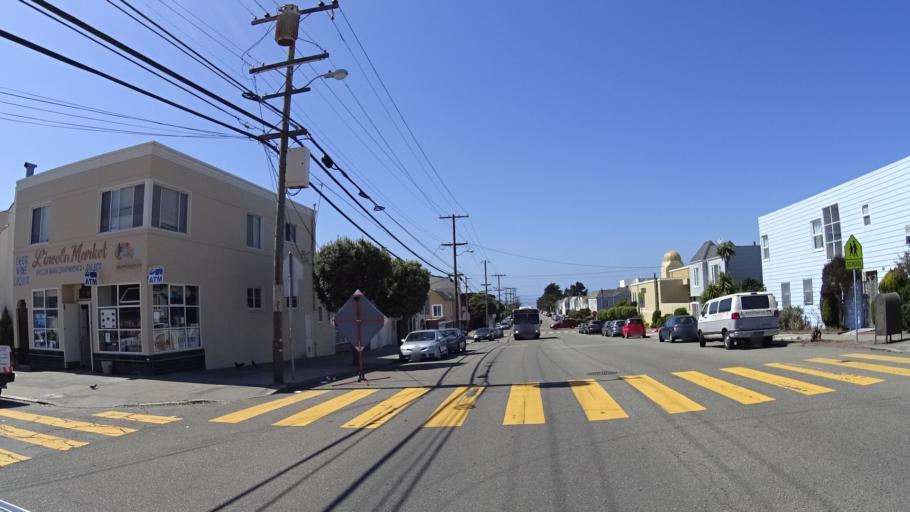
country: US
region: California
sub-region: San Mateo County
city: Daly City
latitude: 37.7485
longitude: -122.4782
